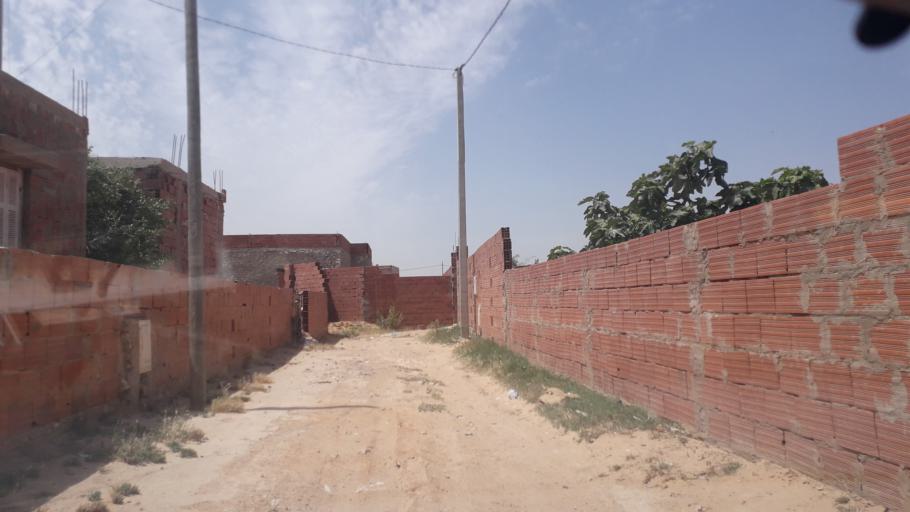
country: TN
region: Safaqis
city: Al Qarmadah
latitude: 34.8451
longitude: 10.7756
